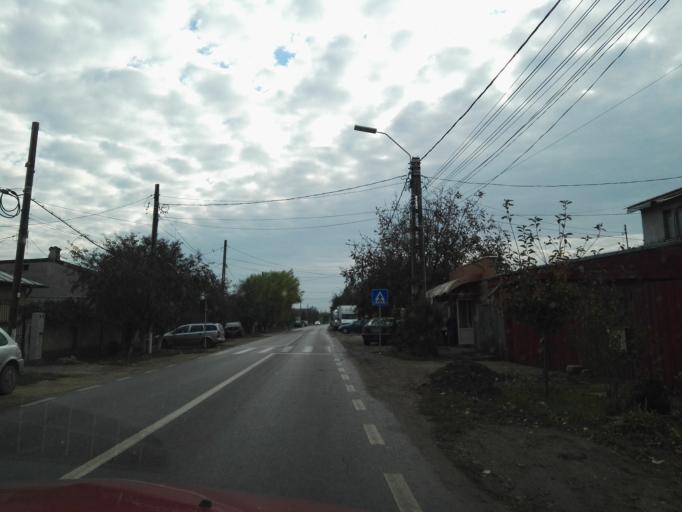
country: RO
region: Ilfov
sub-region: Comuna Magurele
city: Magurele
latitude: 44.3432
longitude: 26.0426
